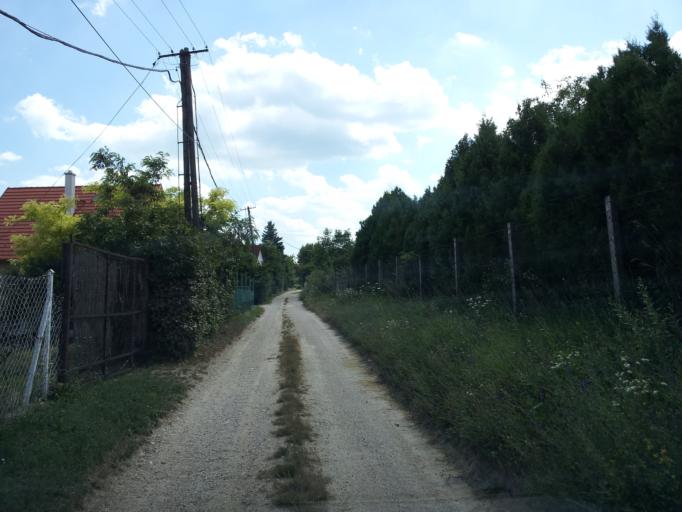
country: HU
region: Veszprem
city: Balatonalmadi
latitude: 47.0590
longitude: 18.0193
